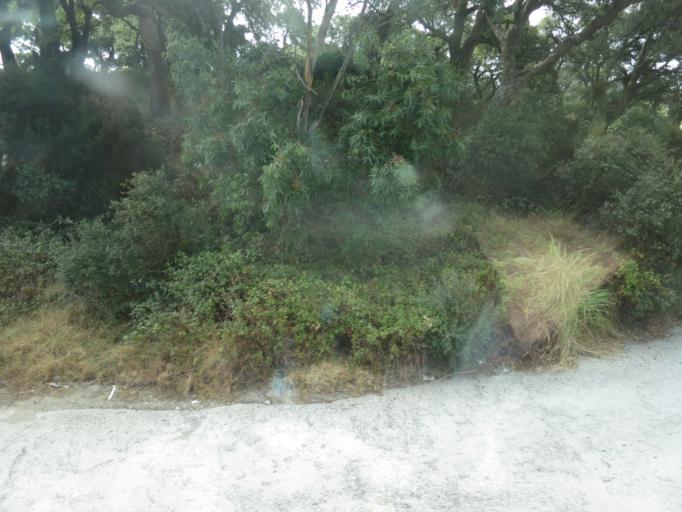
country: ES
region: Andalusia
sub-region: Provincia de Cadiz
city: Algeciras
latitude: 36.0693
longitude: -5.5244
